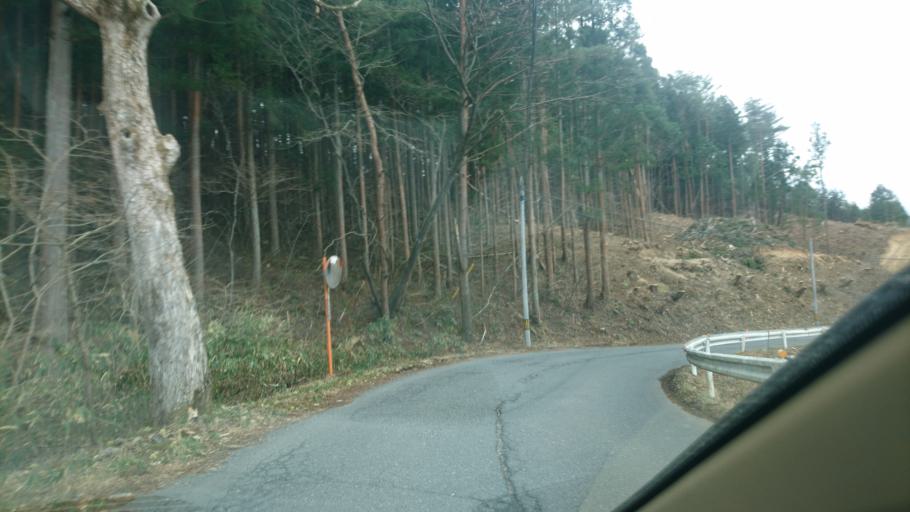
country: JP
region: Miyagi
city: Furukawa
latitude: 38.7255
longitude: 140.8320
